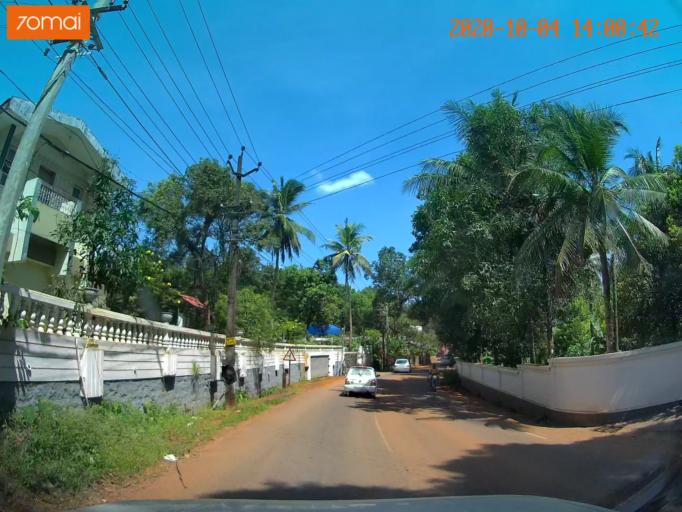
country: IN
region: Kerala
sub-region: Kottayam
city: Lalam
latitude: 9.7122
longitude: 76.6702
